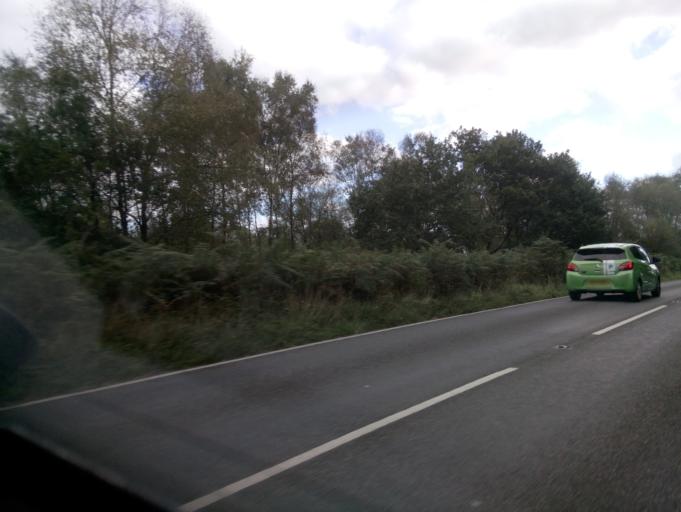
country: GB
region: England
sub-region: Devon
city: Honiton
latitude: 50.7785
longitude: -3.2063
